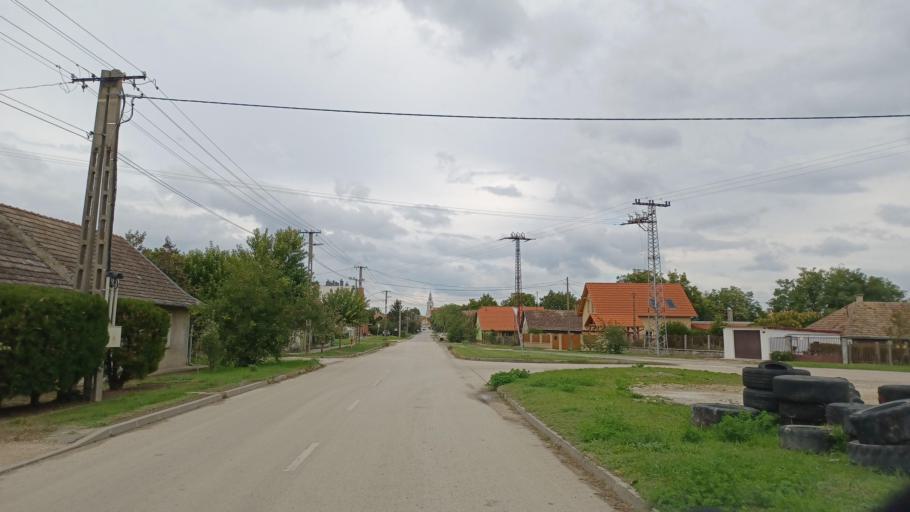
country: HU
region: Tolna
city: Simontornya
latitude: 46.7469
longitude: 18.5579
